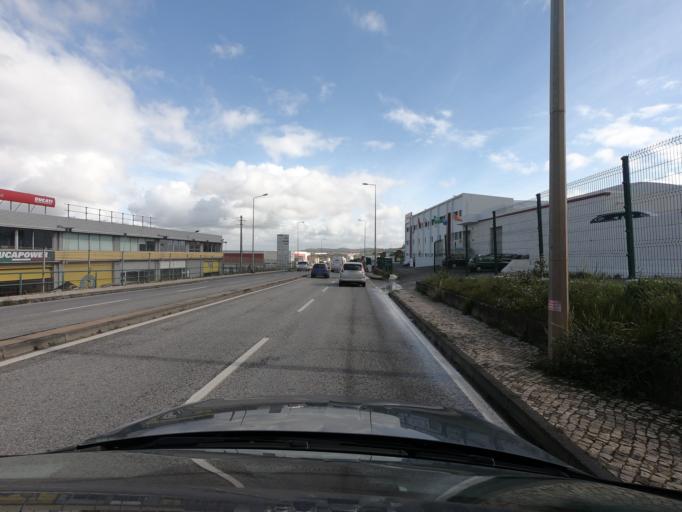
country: PT
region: Lisbon
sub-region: Sintra
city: Cacem
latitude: 38.7601
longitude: -9.3063
